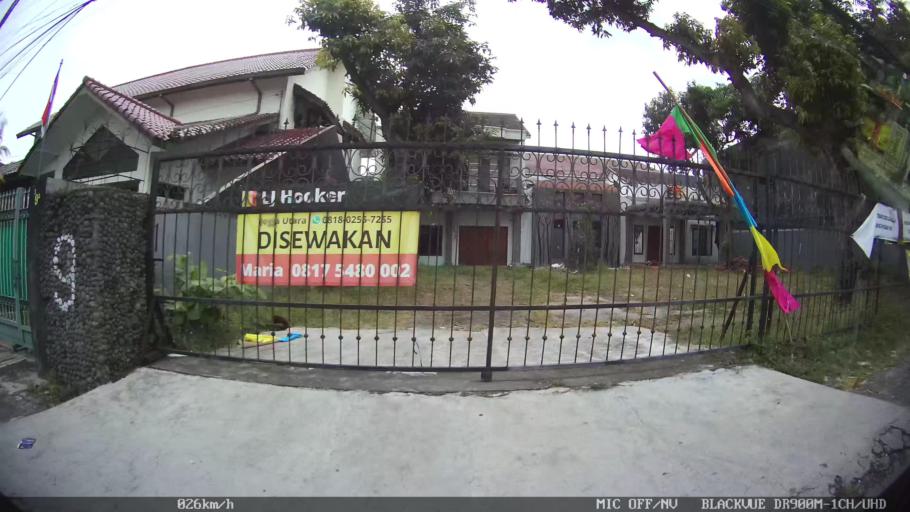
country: ID
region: Daerah Istimewa Yogyakarta
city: Yogyakarta
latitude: -7.7856
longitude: 110.3996
